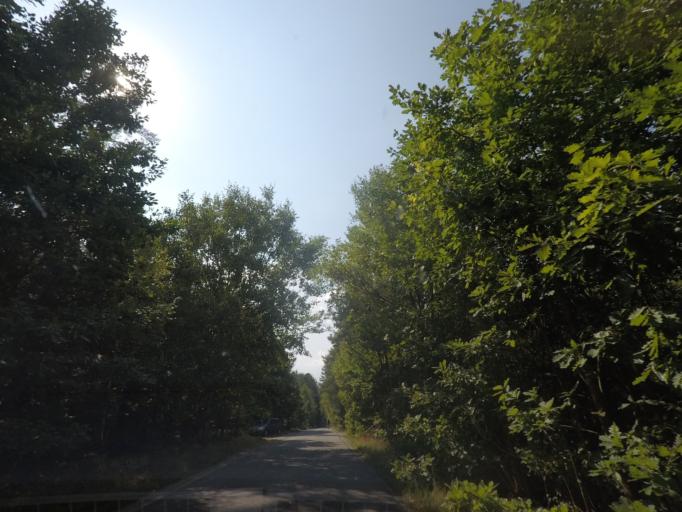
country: CZ
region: Pardubicky
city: Horni Jeleni
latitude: 50.0641
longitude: 16.0779
